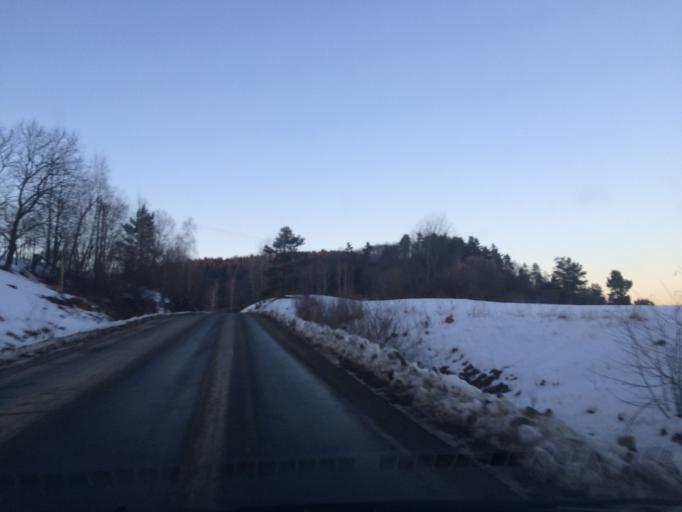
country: PL
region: Subcarpathian Voivodeship
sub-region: Powiat bieszczadzki
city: Ustrzyki Dolne
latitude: 49.3868
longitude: 22.6335
